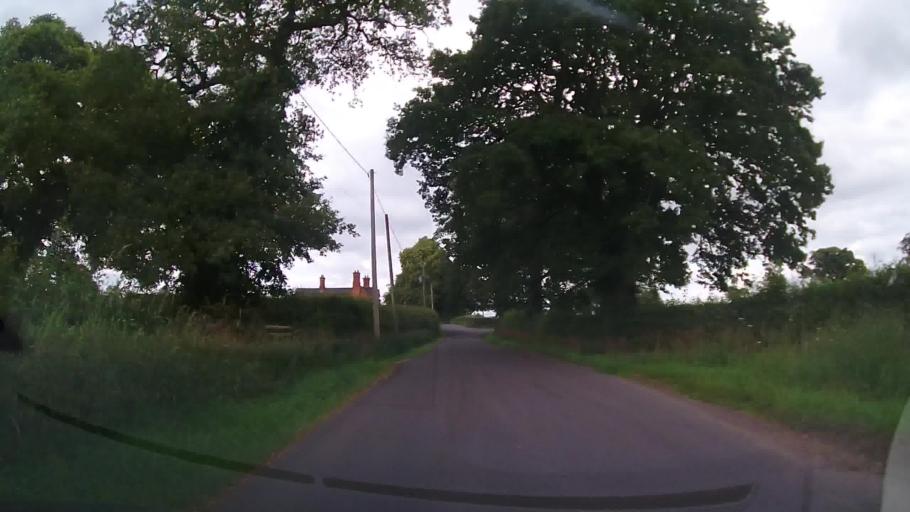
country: GB
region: England
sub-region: Shropshire
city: Wem
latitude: 52.8713
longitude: -2.7375
